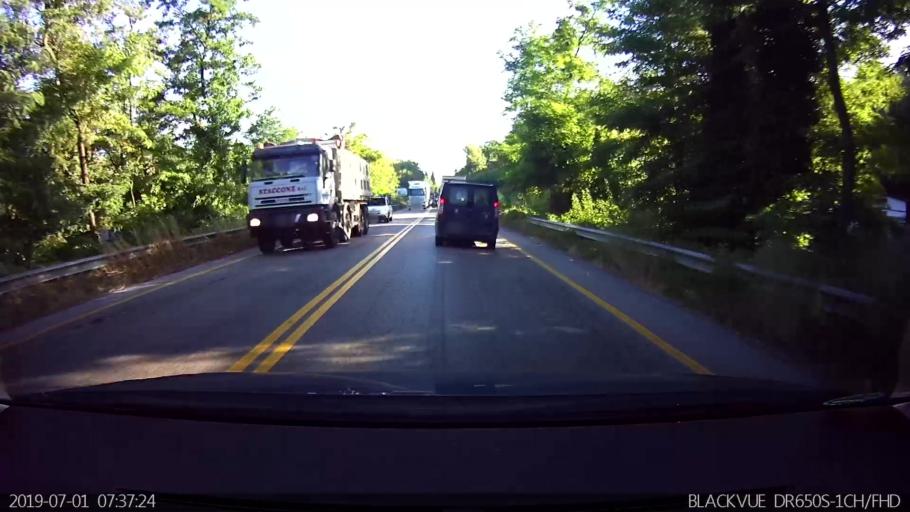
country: IT
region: Latium
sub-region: Provincia di Frosinone
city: Giuliano di Roma
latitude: 41.5377
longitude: 13.2669
